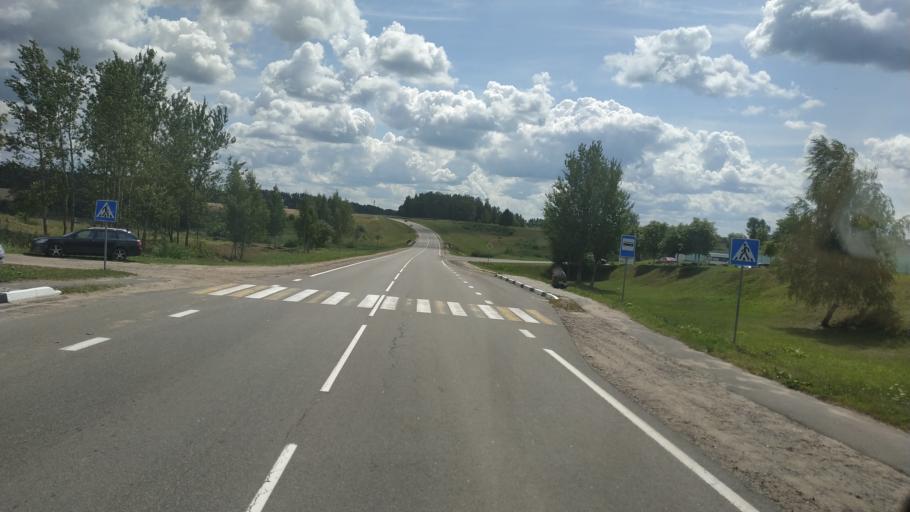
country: BY
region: Mogilev
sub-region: Mahilyowski Rayon
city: Veyno
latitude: 53.8372
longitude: 30.3987
